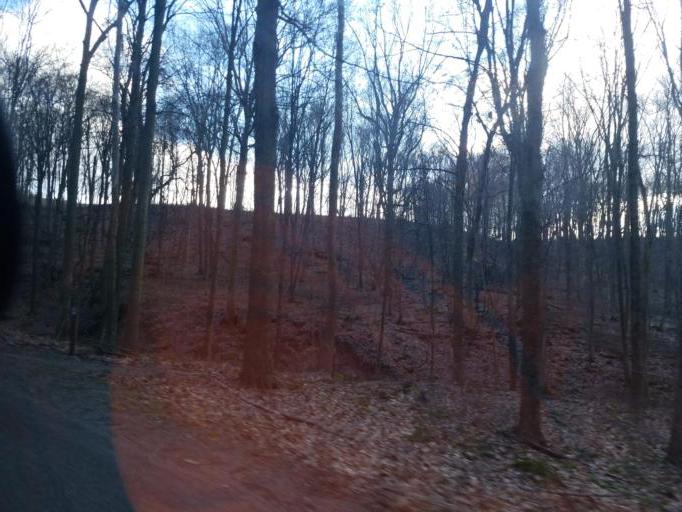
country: US
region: Ohio
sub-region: Sandusky County
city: Bellville
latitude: 40.6257
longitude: -82.3781
